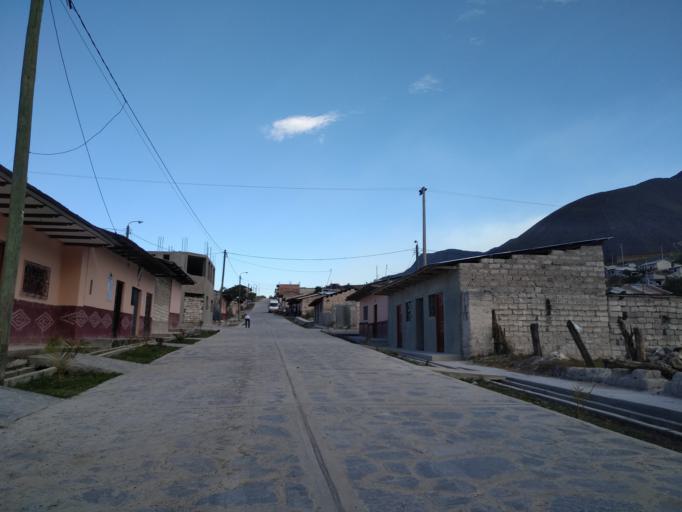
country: PE
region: Amazonas
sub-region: Provincia de Luya
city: Tingo
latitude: -6.3731
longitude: -77.9113
